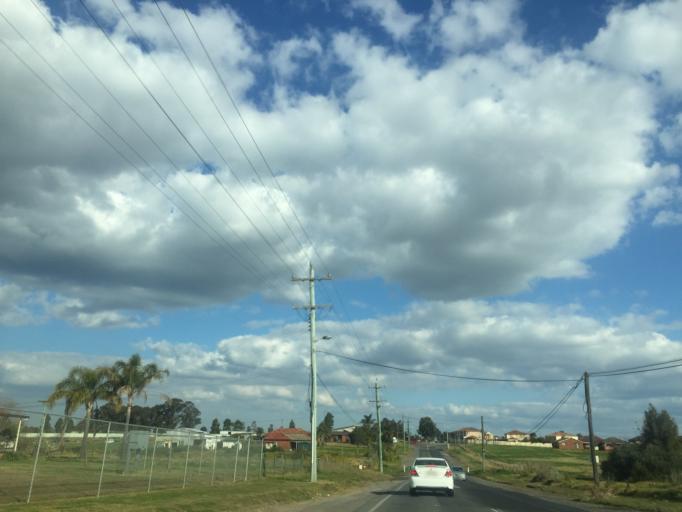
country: AU
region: New South Wales
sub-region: Blacktown
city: Quakers Hill
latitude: -33.7101
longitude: 150.8935
